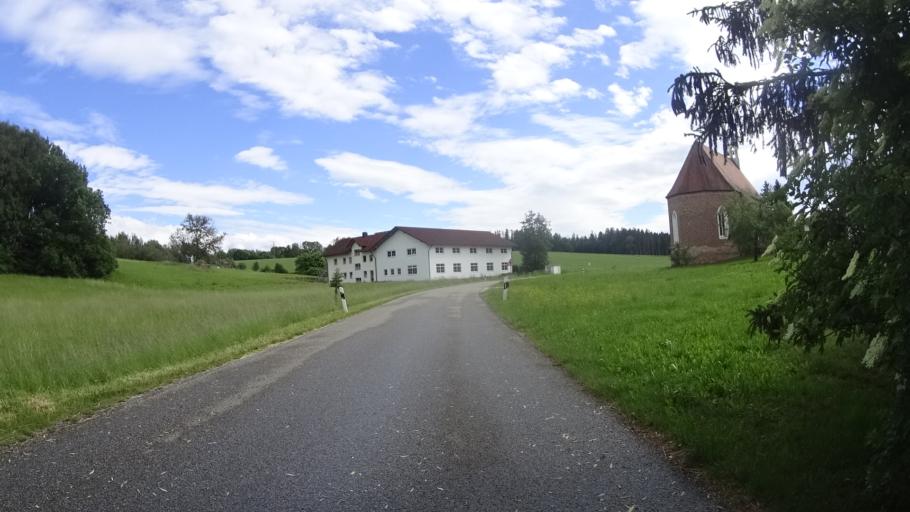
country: DE
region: Bavaria
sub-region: Lower Bavaria
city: Bodenkirchen
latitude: 48.3903
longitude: 12.3528
